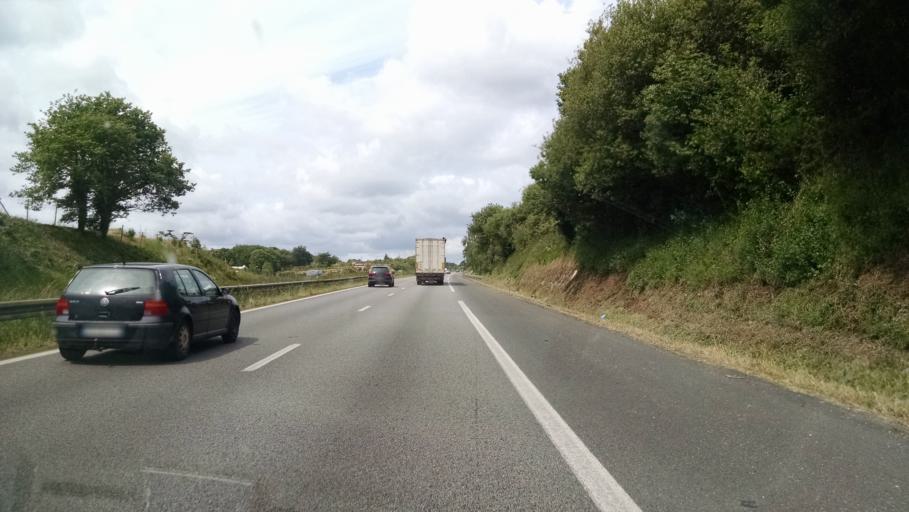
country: FR
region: Brittany
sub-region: Departement du Morbihan
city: Arradon
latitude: 47.6607
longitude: -2.8182
